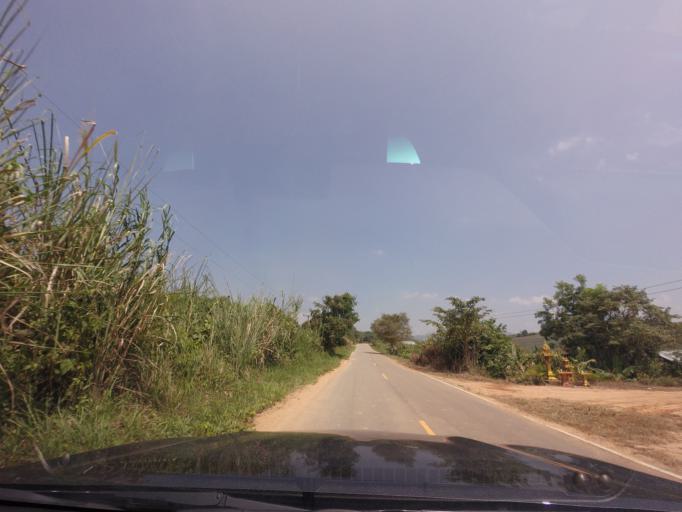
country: TH
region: Loei
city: Na Haeo
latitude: 17.5422
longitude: 100.8782
